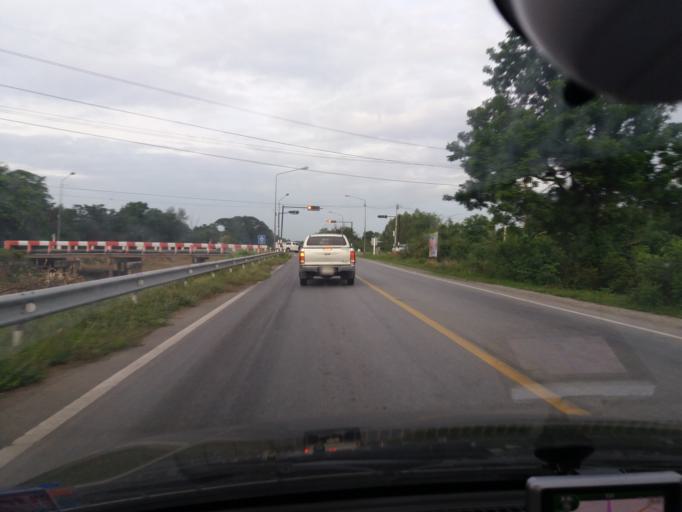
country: TH
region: Suphan Buri
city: Don Chedi
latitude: 14.5332
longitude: 99.9331
